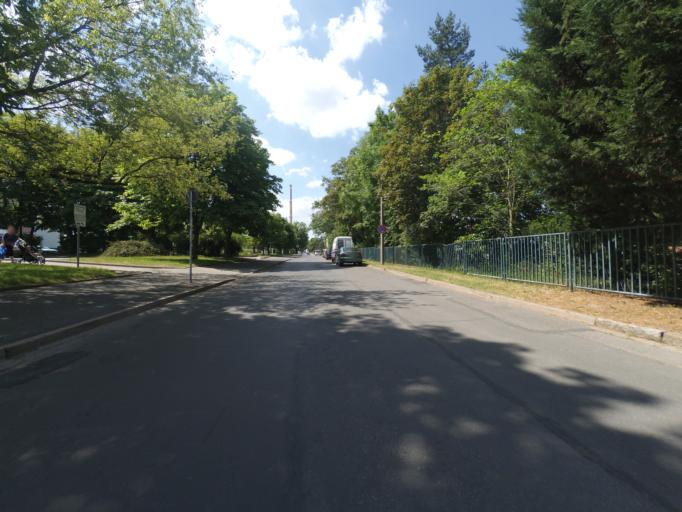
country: DE
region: Saxony
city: Dresden
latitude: 51.0314
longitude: 13.7893
